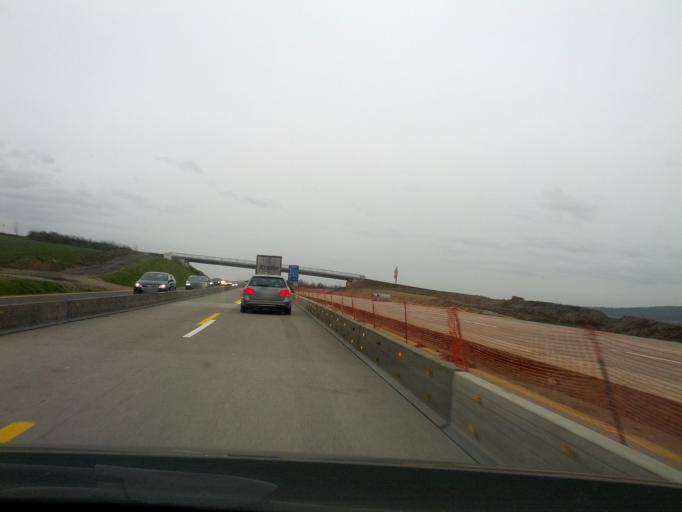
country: DE
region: Lower Saxony
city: Bockenem
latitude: 51.9542
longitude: 10.1405
